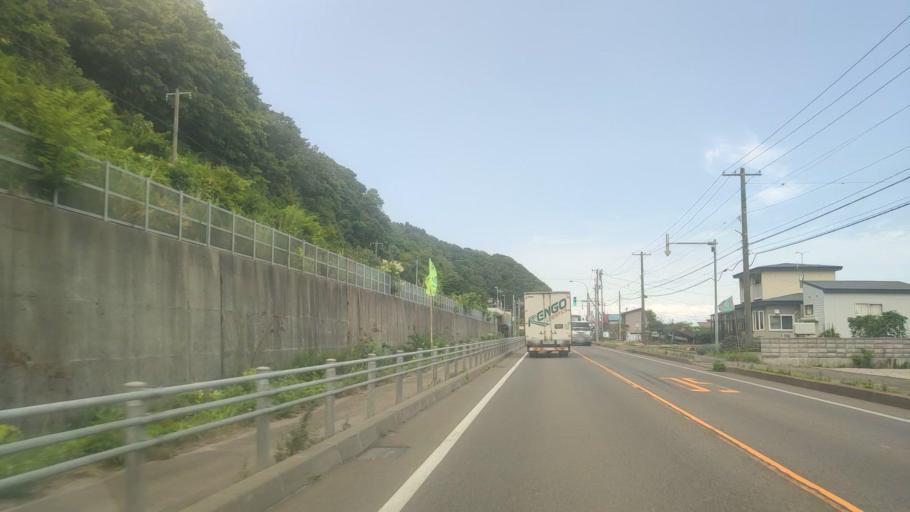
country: JP
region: Hokkaido
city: Nanae
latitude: 42.1591
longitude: 140.4731
